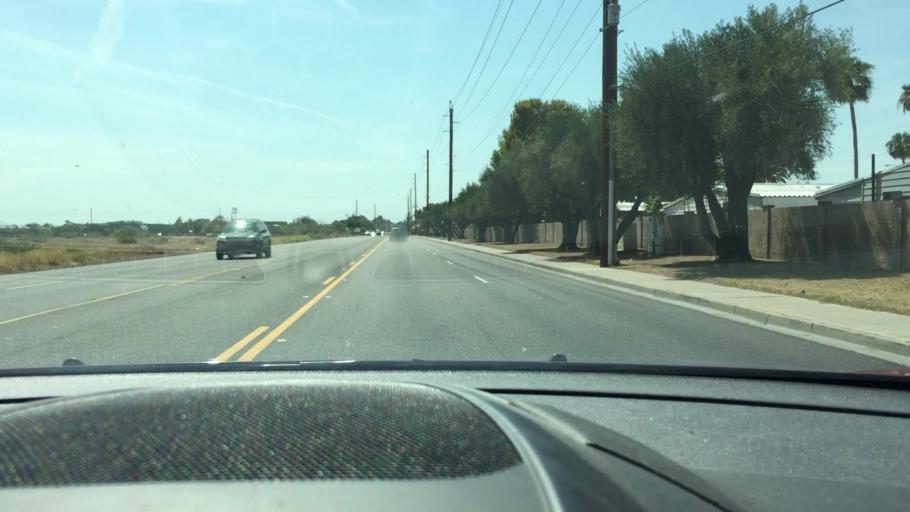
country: US
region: Arizona
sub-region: Maricopa County
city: Tempe
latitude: 33.4508
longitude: -111.9042
